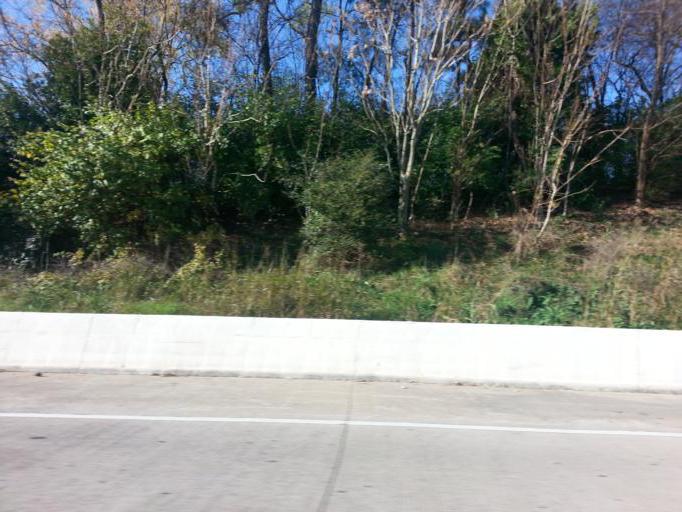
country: US
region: Tennessee
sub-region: Knox County
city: Knoxville
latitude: 35.9796
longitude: -83.9372
